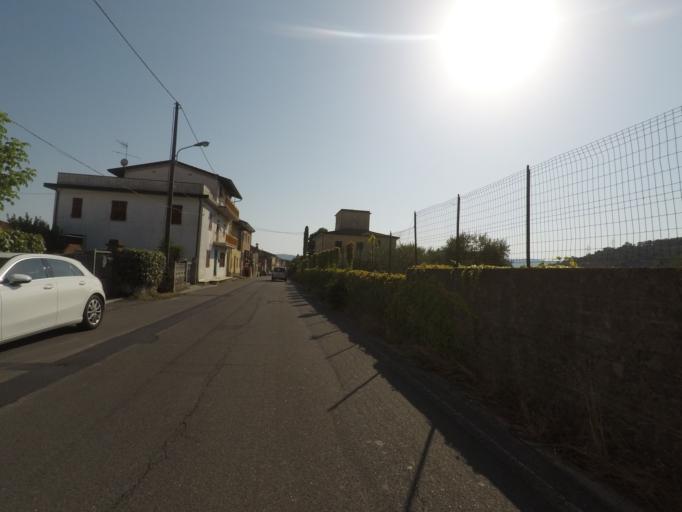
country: IT
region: Liguria
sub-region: Provincia di La Spezia
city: Casano-Dogana-Isola
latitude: 44.0825
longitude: 10.0365
